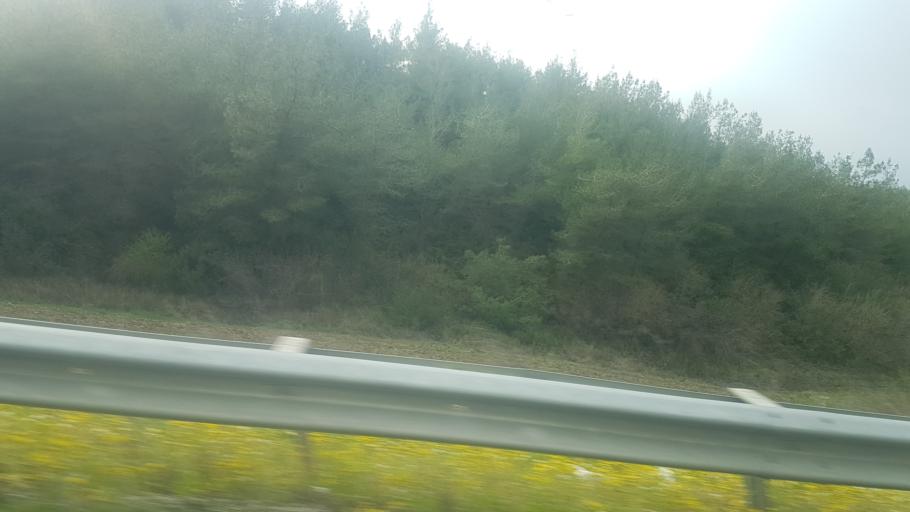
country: TR
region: Mersin
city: Yenice
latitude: 37.0795
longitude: 35.1732
